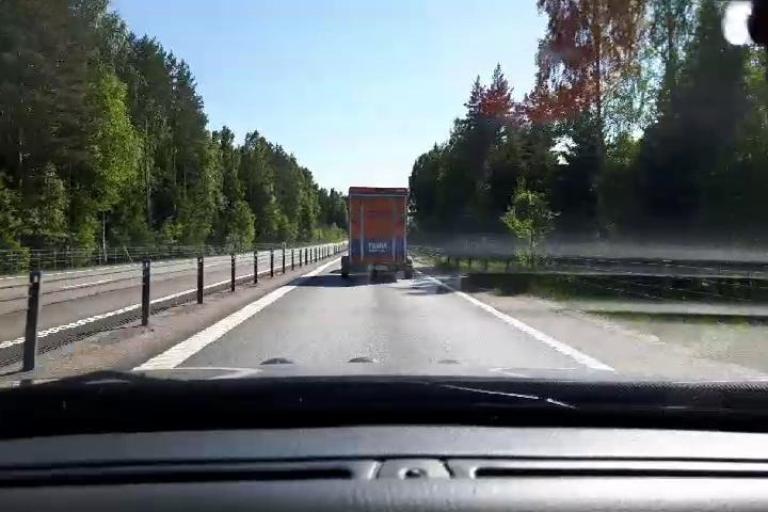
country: SE
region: Gaevleborg
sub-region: Soderhamns Kommun
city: Ljusne
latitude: 61.1413
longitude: 17.0293
